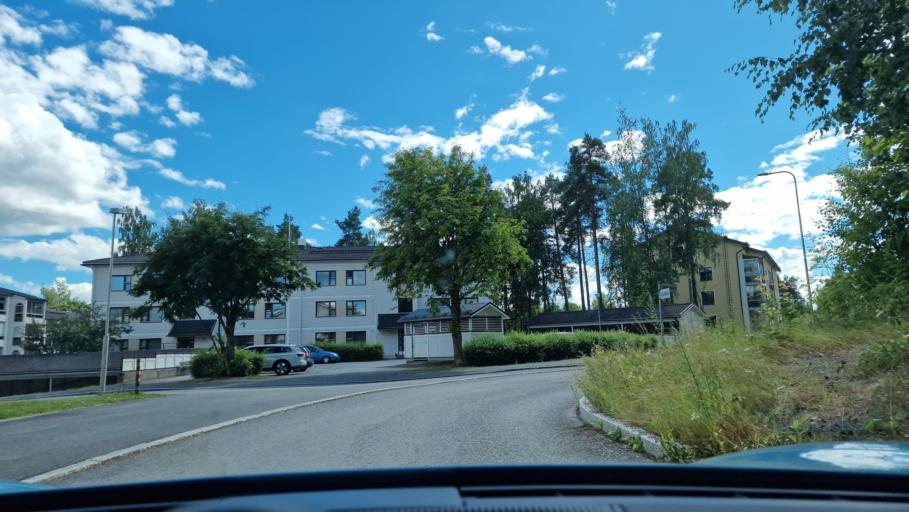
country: FI
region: Pirkanmaa
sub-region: Etelae-Pirkanmaa
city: Valkeakoski
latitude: 61.2723
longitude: 24.0191
